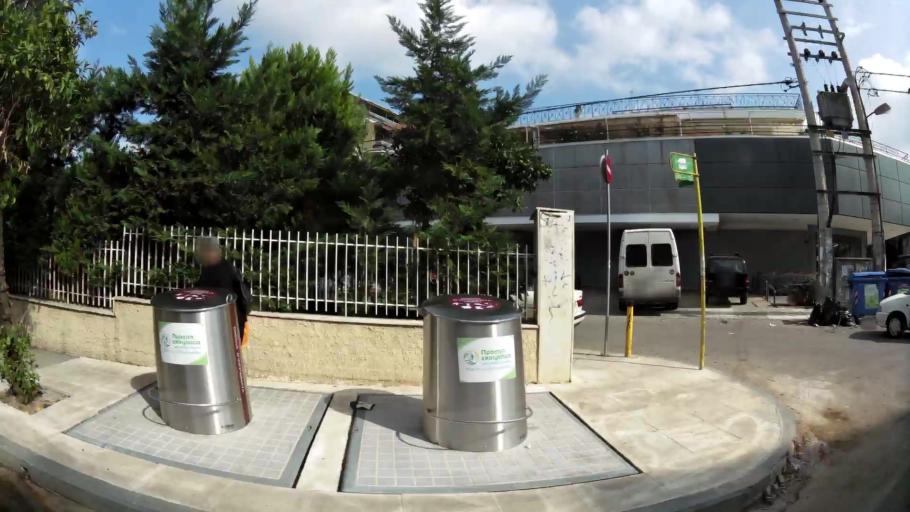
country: GR
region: Attica
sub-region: Nomarchia Athinas
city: Cholargos
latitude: 37.9940
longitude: 23.8013
